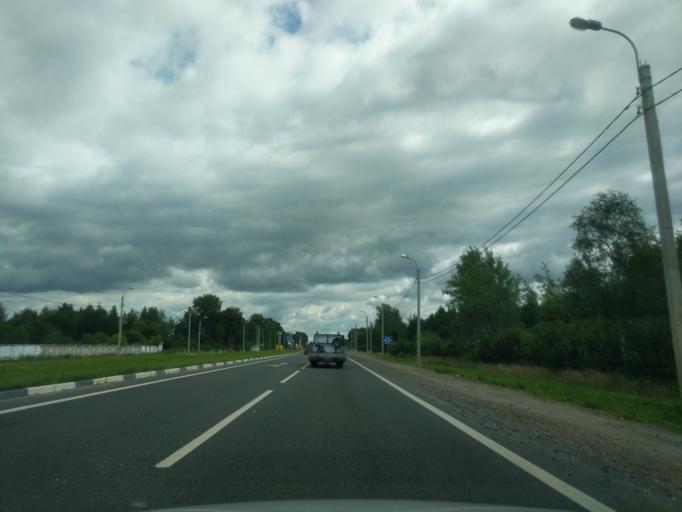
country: RU
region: Jaroslavl
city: Tunoshna
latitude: 57.5407
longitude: 39.9848
